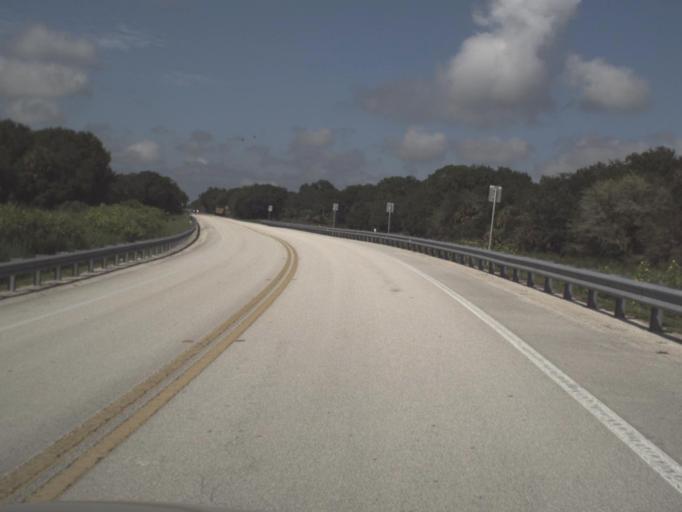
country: US
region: Florida
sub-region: Sarasota County
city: Warm Mineral Springs
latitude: 27.1956
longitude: -82.2018
